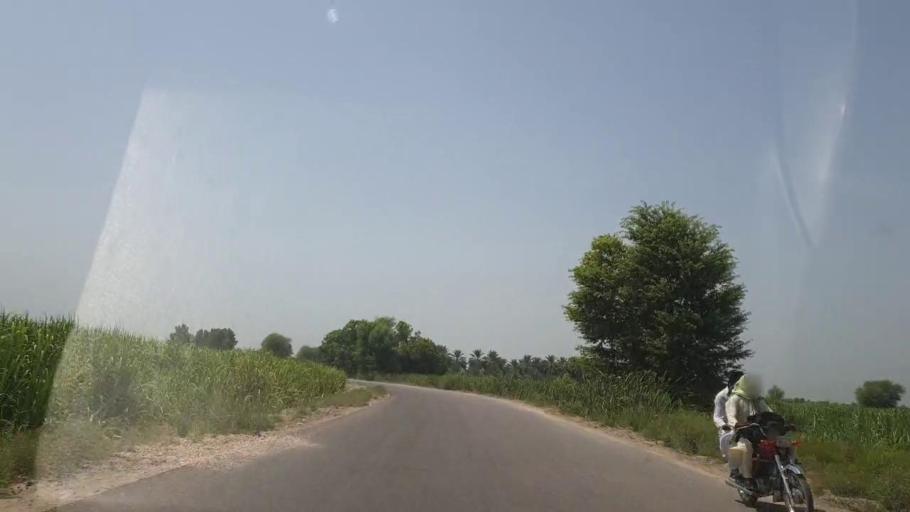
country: PK
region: Sindh
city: Ranipur
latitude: 27.2933
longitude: 68.6045
